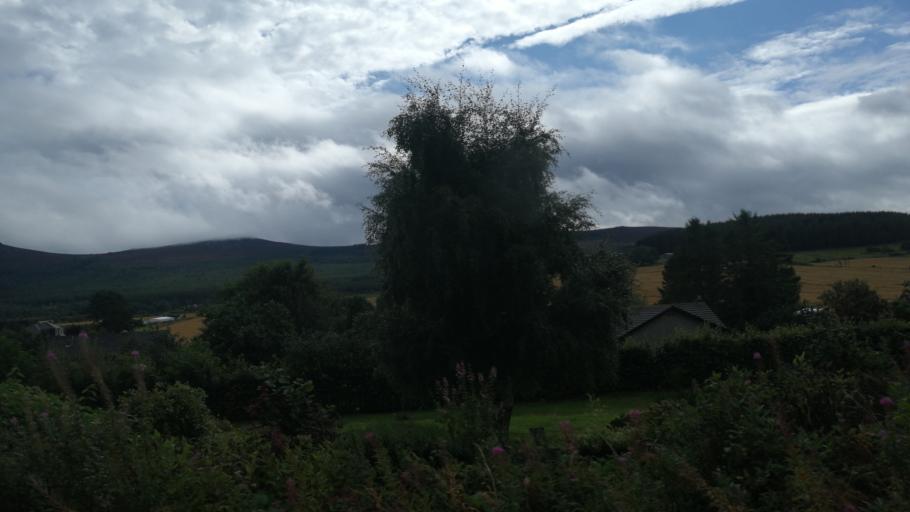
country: GB
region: Scotland
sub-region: Aberdeenshire
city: Insch
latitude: 57.3241
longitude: -2.5660
